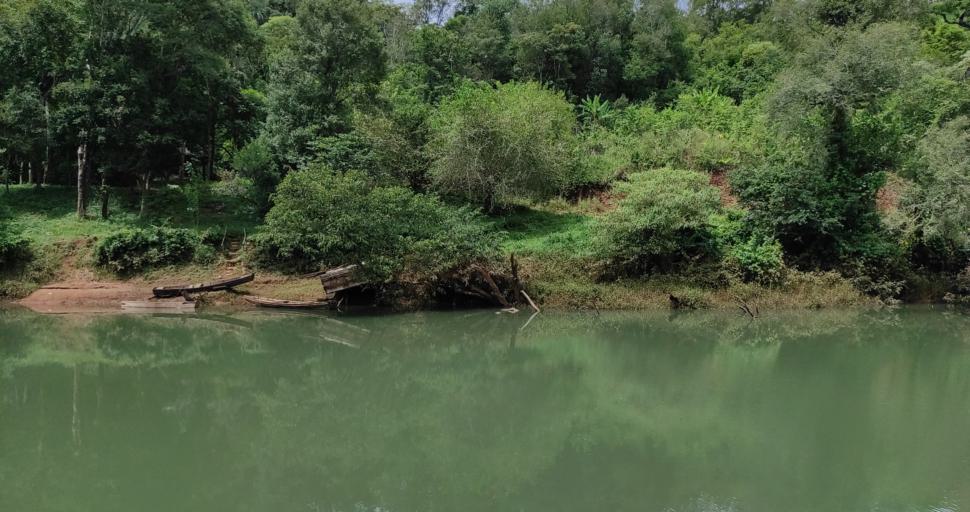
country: AR
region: Misiones
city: El Soberbio
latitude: -27.2832
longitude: -54.2118
